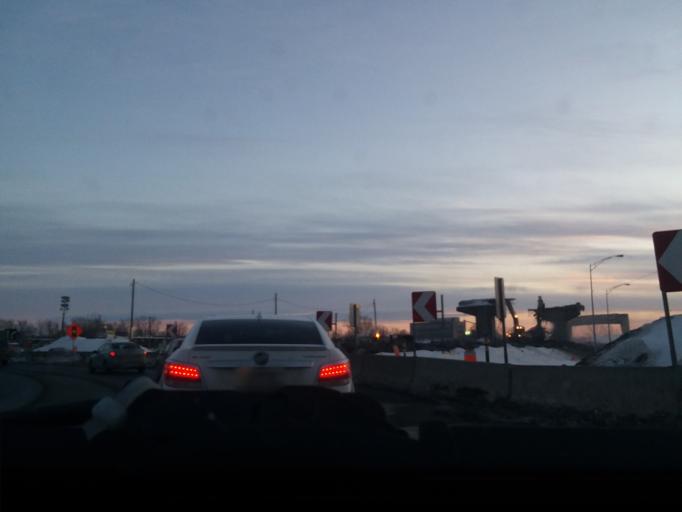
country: CA
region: Quebec
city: Montreal-Ouest
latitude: 45.4525
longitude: -73.6294
